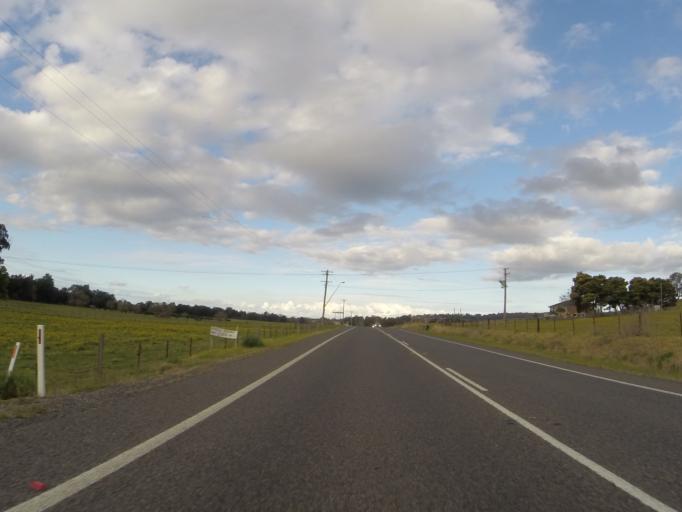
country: AU
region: New South Wales
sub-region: Shellharbour
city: Calderwood
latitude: -34.5771
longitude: 150.7385
